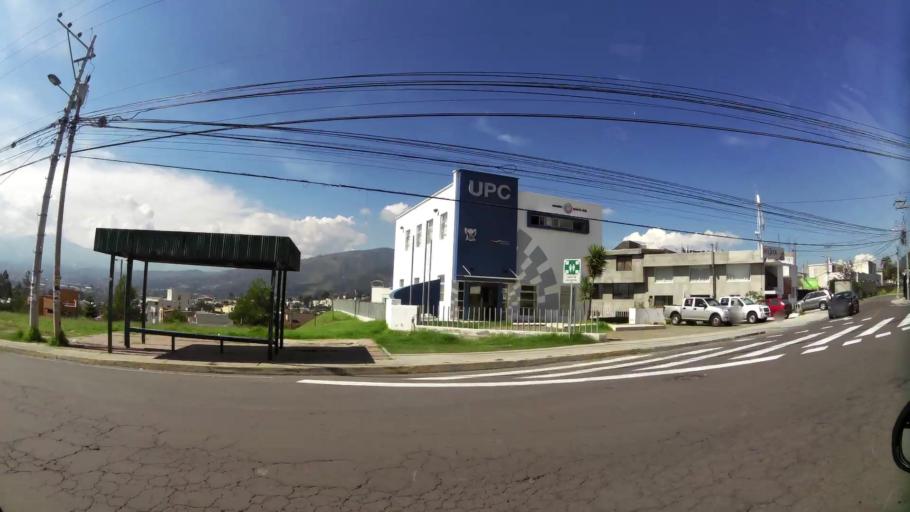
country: EC
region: Pichincha
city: Quito
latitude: -0.2030
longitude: -78.4397
